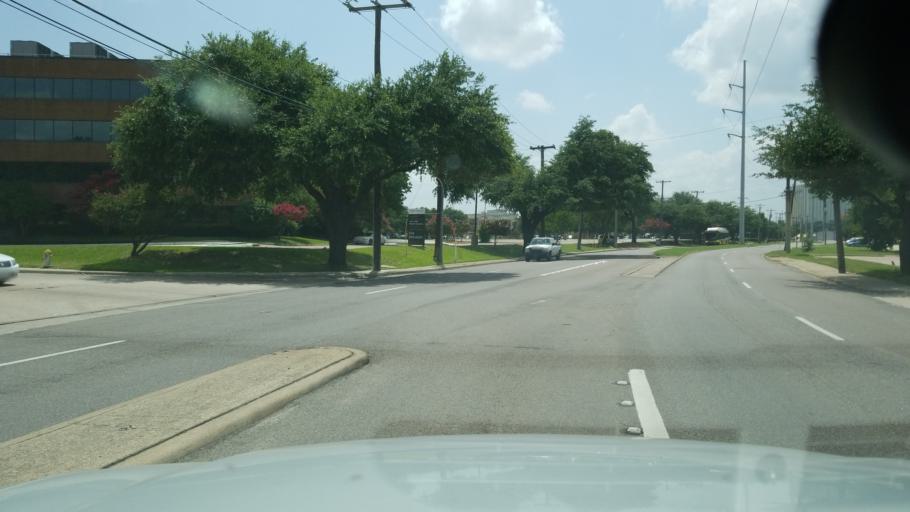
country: US
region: Texas
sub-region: Dallas County
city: University Park
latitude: 32.8260
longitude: -96.8667
